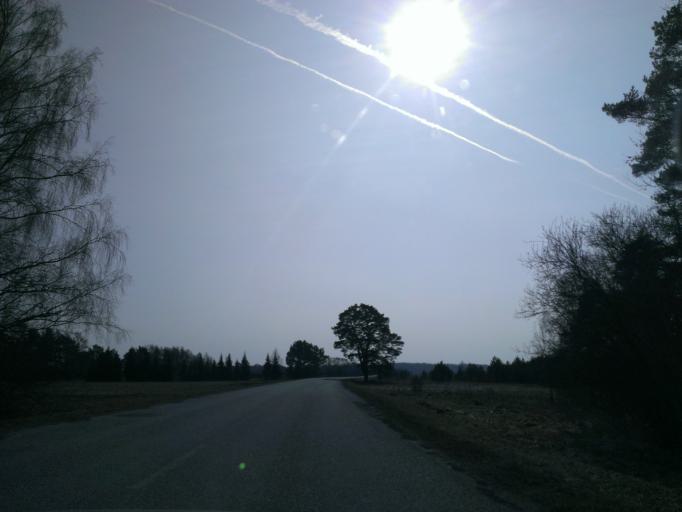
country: EE
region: Saare
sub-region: Orissaare vald
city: Orissaare
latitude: 58.5446
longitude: 23.1136
